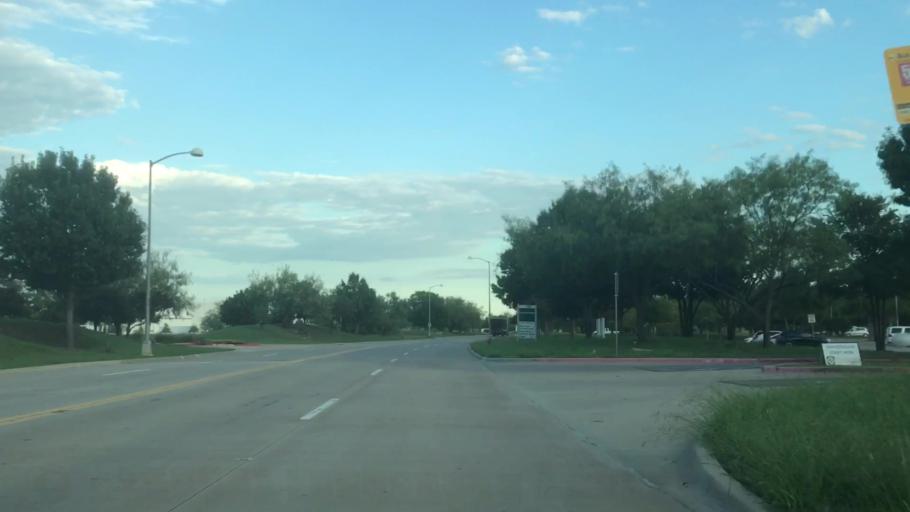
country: US
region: Texas
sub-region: Dallas County
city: Coppell
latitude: 32.9420
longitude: -97.0269
